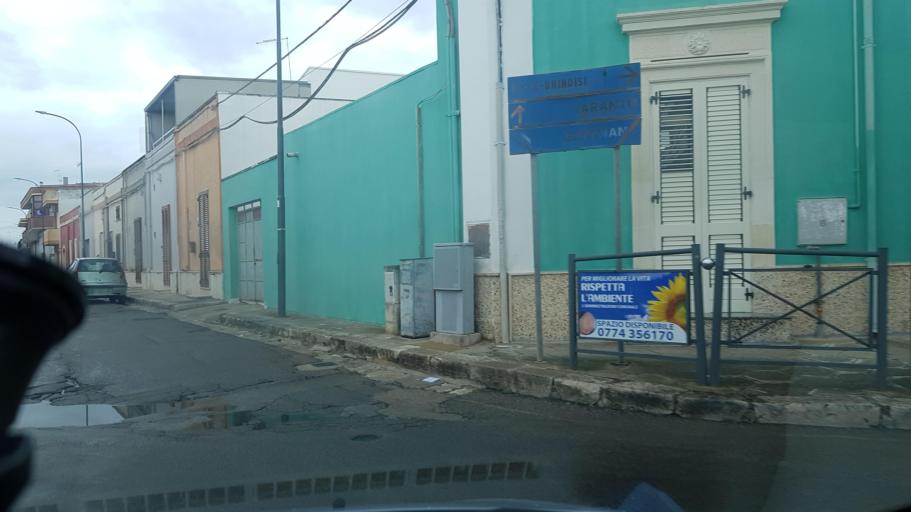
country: IT
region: Apulia
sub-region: Provincia di Lecce
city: Salice Salentino
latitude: 40.3874
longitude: 17.9601
